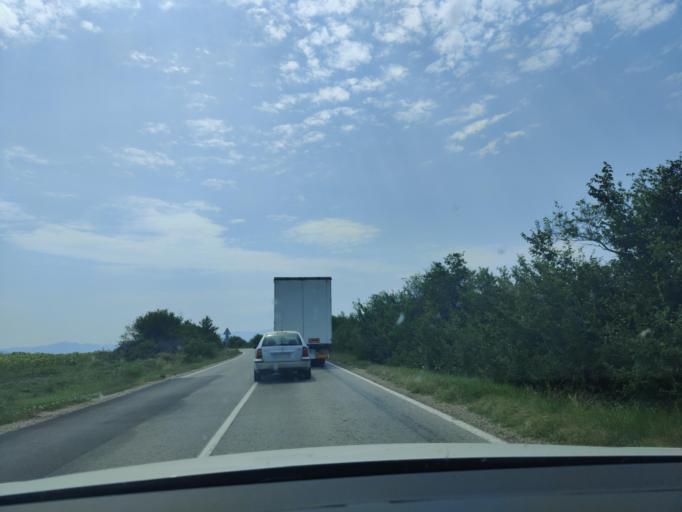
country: BG
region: Vidin
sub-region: Obshtina Ruzhintsi
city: Ruzhintsi
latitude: 43.6708
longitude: 22.7727
